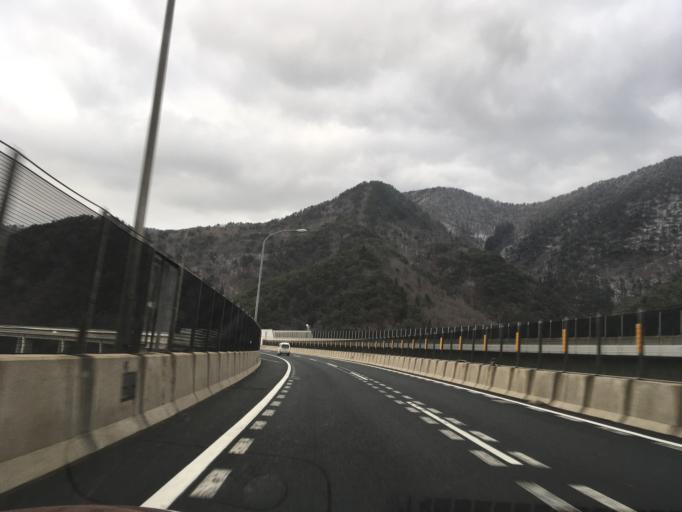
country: JP
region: Yamagata
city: Yamagata-shi
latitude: 38.2336
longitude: 140.4096
